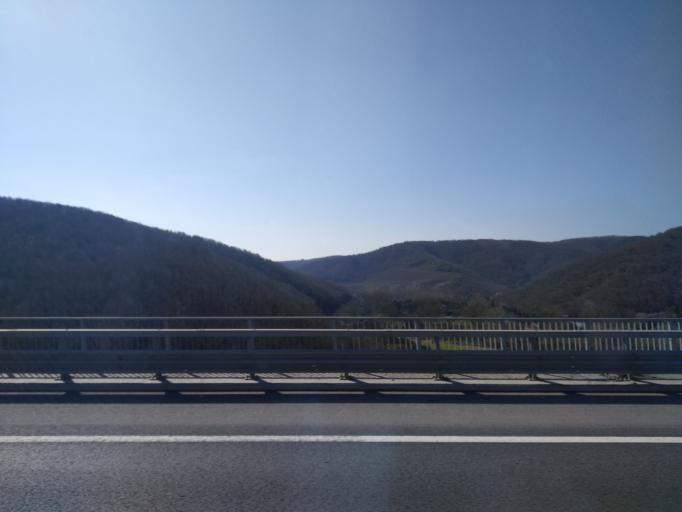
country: TR
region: Istanbul
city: Mahmut Sevket Pasa
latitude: 41.1523
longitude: 29.2689
